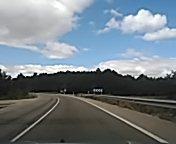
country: ES
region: Castille and Leon
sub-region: Provincia de Burgos
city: Hontoria del Pinar
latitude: 41.8478
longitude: -3.1157
